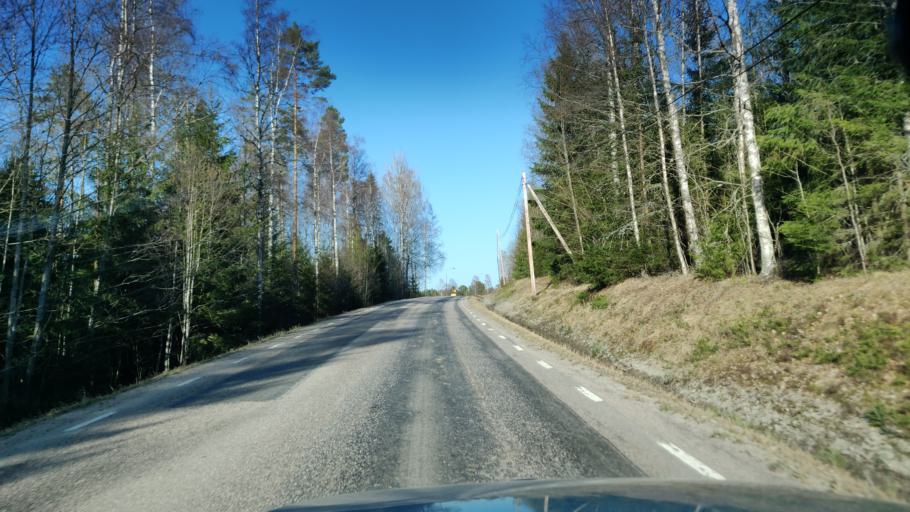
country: SE
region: Vaermland
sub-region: Sunne Kommun
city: Sunne
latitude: 59.9923
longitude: 13.2806
